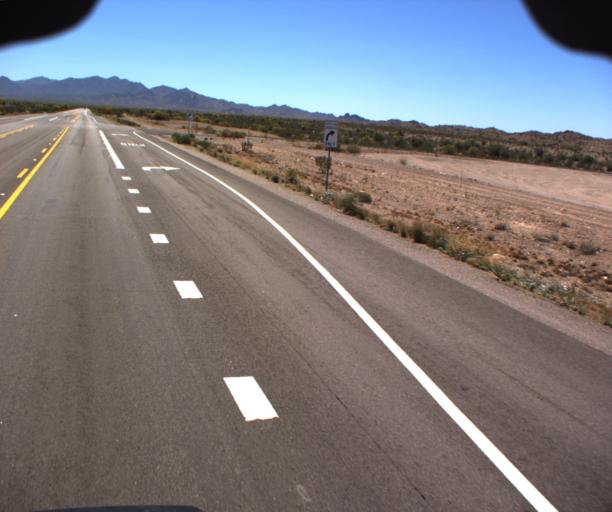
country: US
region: Arizona
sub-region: Mohave County
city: Desert Hills
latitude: 34.7217
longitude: -114.3130
